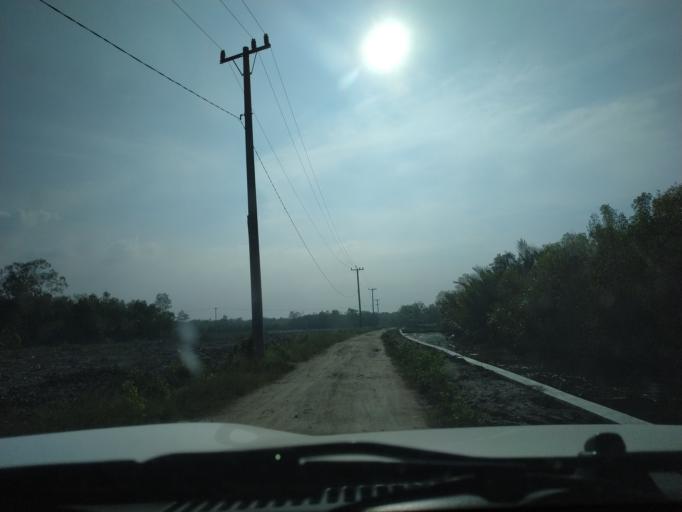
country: ID
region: North Sumatra
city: Teluk Nibung
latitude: 3.1028
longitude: 99.7755
